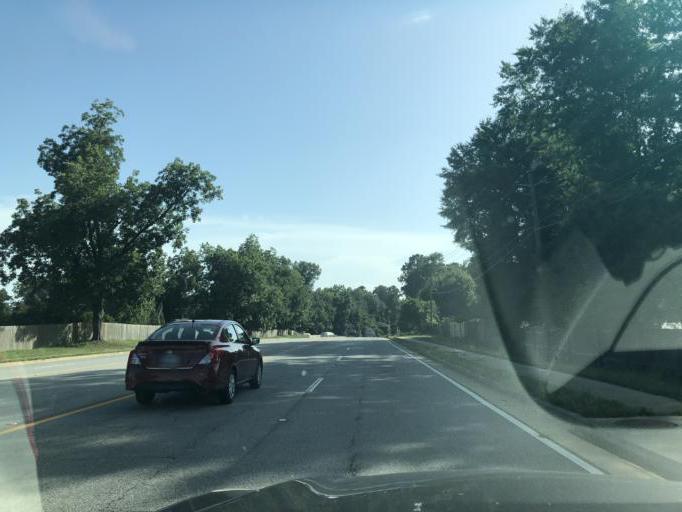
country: US
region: Georgia
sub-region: Muscogee County
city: Columbus
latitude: 32.5040
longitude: -84.8983
